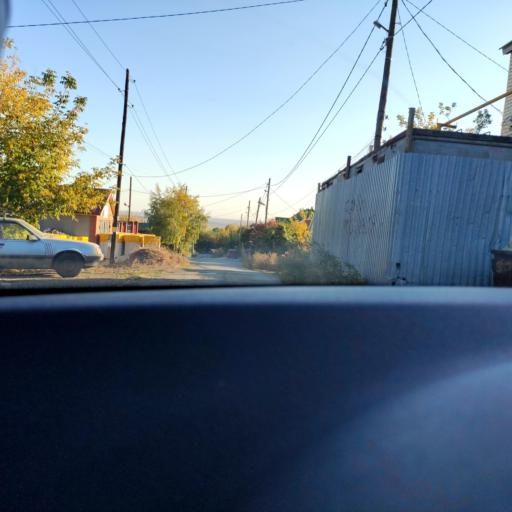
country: RU
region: Samara
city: Samara
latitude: 53.1862
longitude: 50.1888
